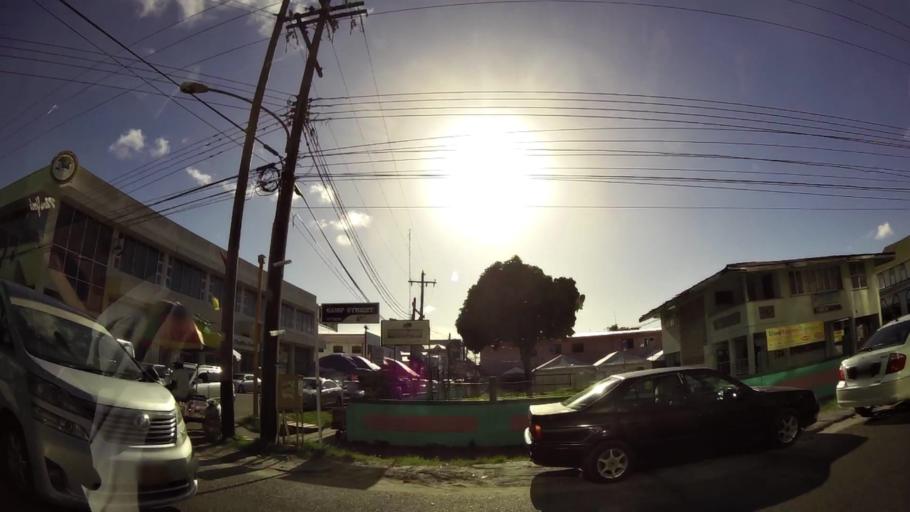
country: GY
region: Demerara-Mahaica
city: Georgetown
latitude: 6.8112
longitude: -58.1605
